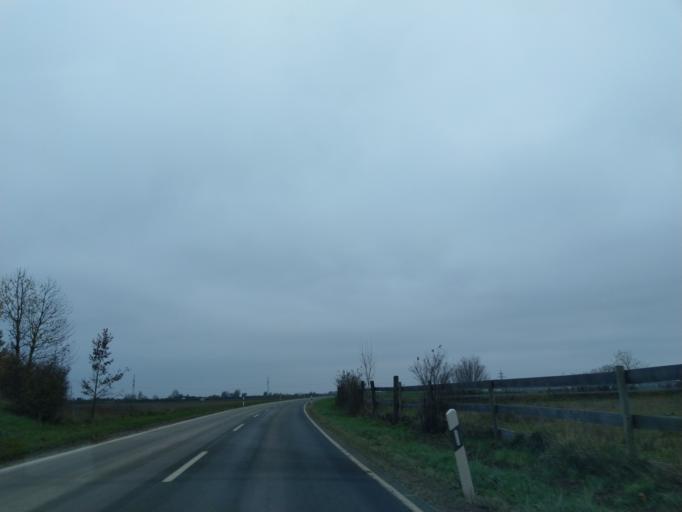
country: DE
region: Bavaria
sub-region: Lower Bavaria
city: Otzing
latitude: 48.7865
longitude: 12.8250
